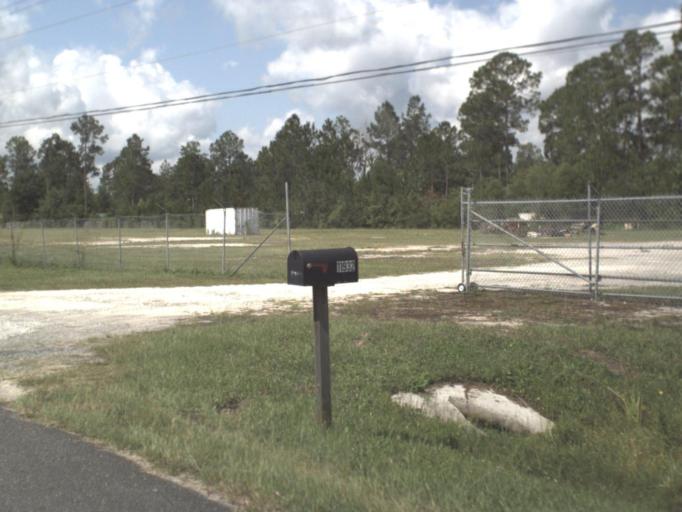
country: US
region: Florida
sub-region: Baker County
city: Macclenny
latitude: 30.3015
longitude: -82.1259
